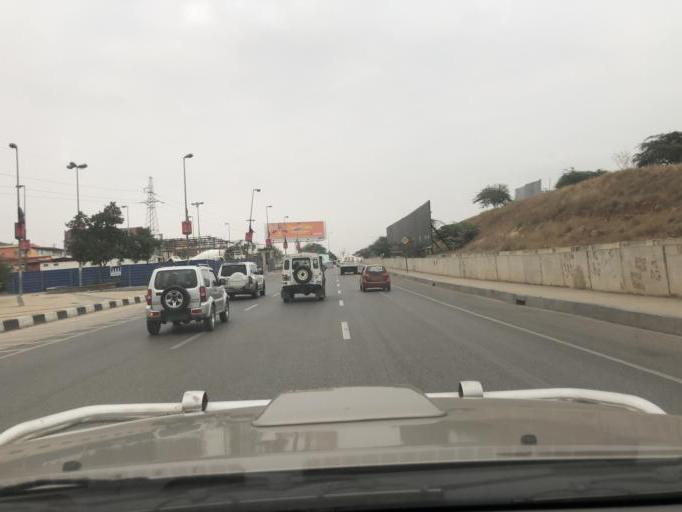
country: AO
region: Luanda
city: Luanda
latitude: -8.8802
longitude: 13.1867
